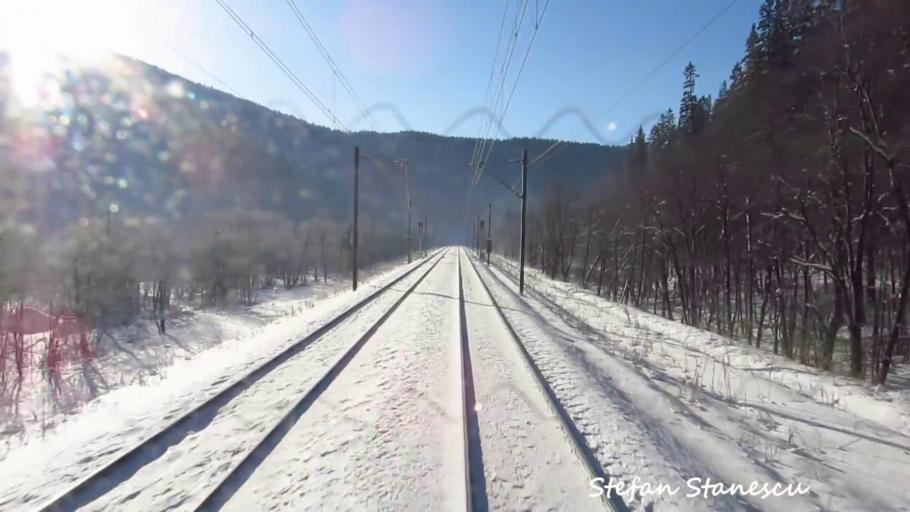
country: RO
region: Prahova
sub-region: Oras Azuga
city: Azuga
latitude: 45.4640
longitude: 25.5608
